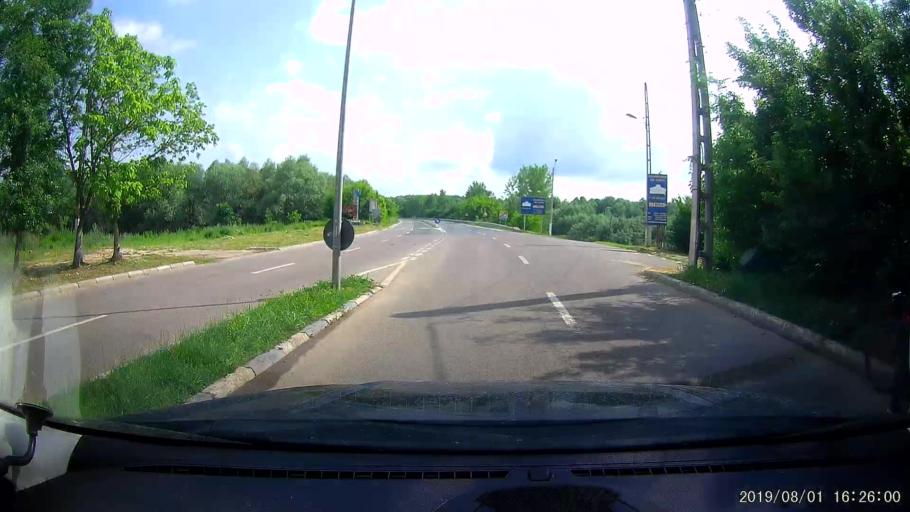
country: RO
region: Calarasi
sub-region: Municipiul Calarasi
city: Calarasi
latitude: 44.1878
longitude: 27.3226
